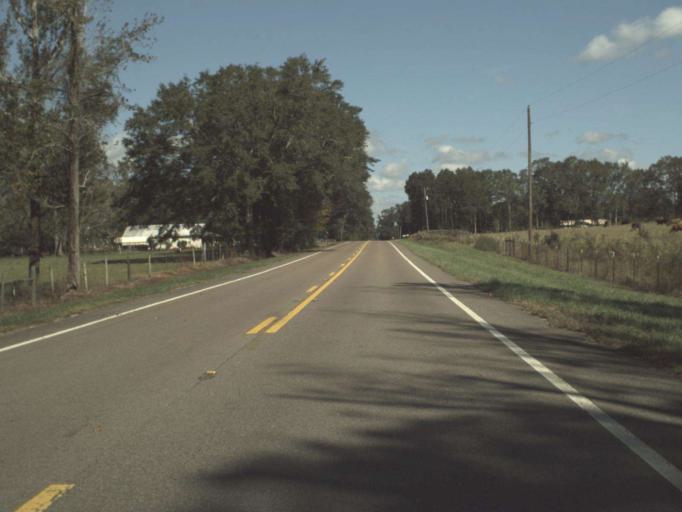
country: US
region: Alabama
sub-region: Geneva County
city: Samson
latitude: 30.9803
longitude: -86.1344
